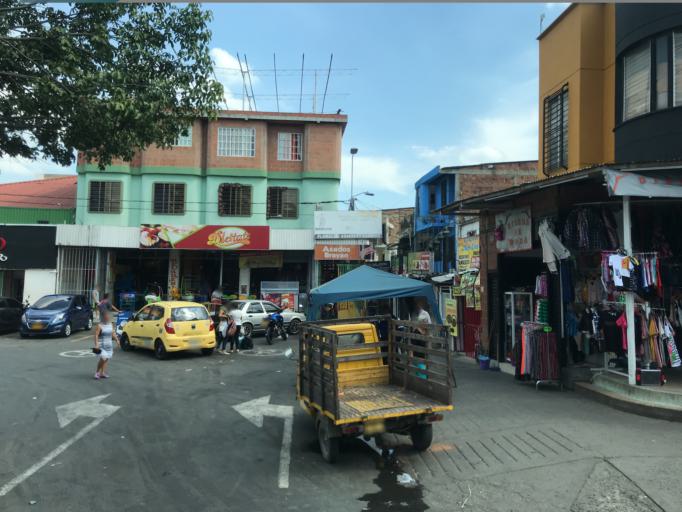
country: CO
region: Valle del Cauca
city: Cali
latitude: 3.4940
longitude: -76.4949
